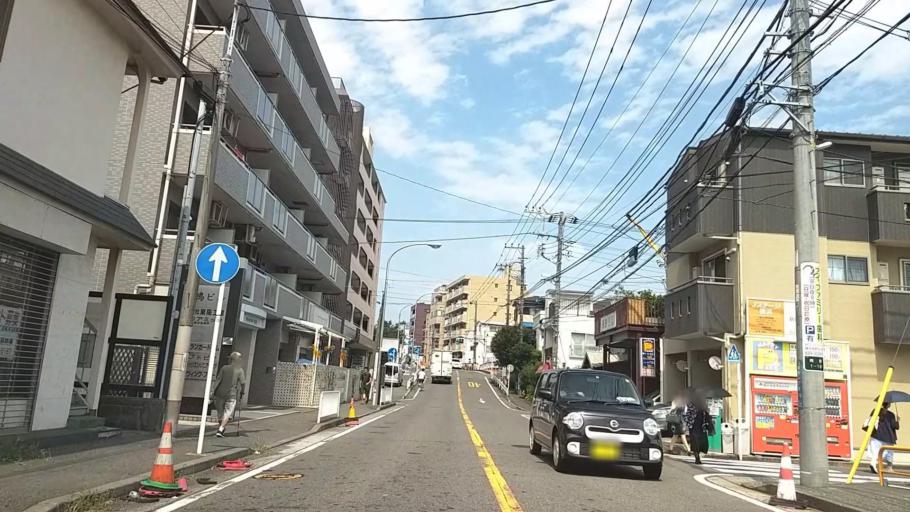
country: JP
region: Kanagawa
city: Yokohama
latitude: 35.4627
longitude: 139.6132
